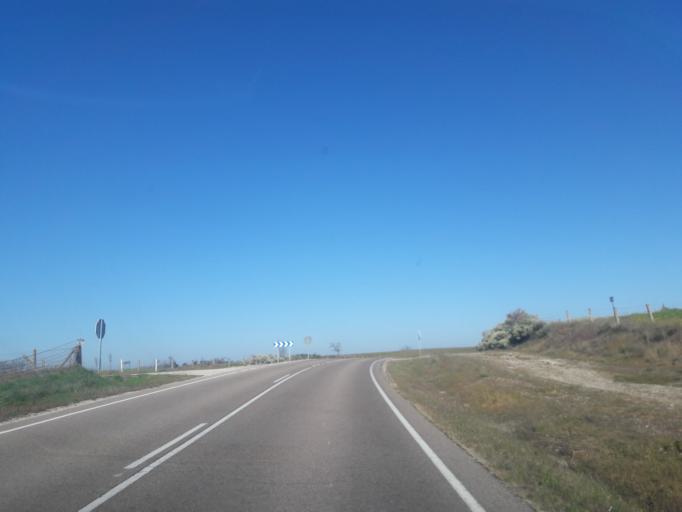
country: ES
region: Castille and Leon
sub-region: Provincia de Salamanca
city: Valderrodrigo
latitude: 41.0728
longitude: -6.5310
